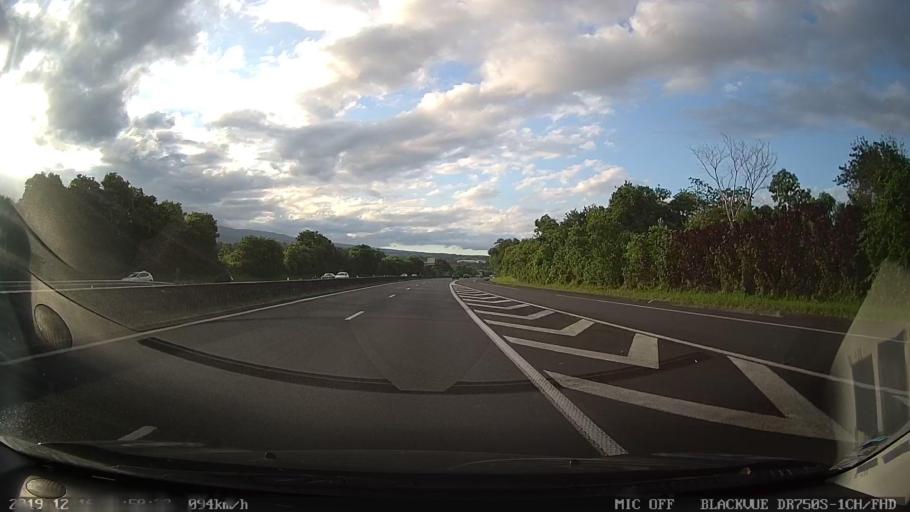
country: RE
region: Reunion
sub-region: Reunion
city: Bras-Panon
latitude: -21.0131
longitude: 55.6915
